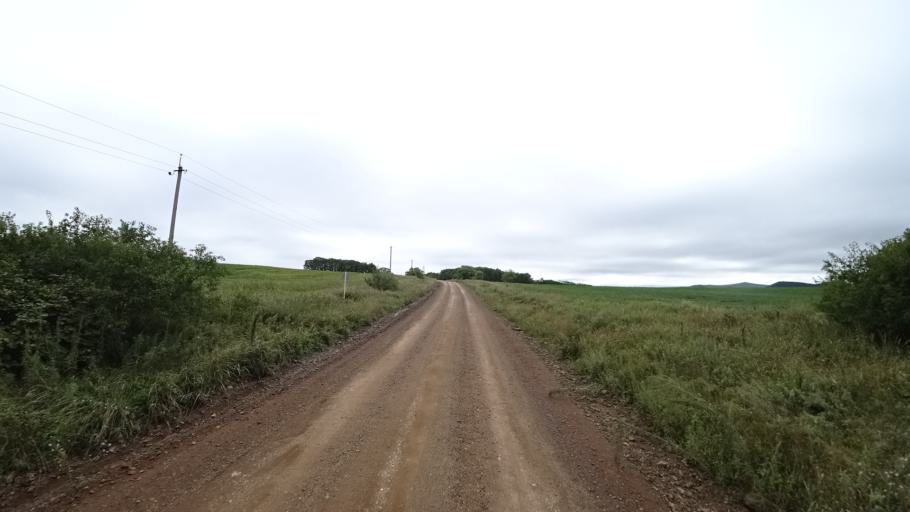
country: RU
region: Primorskiy
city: Lyalichi
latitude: 44.0625
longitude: 132.4776
